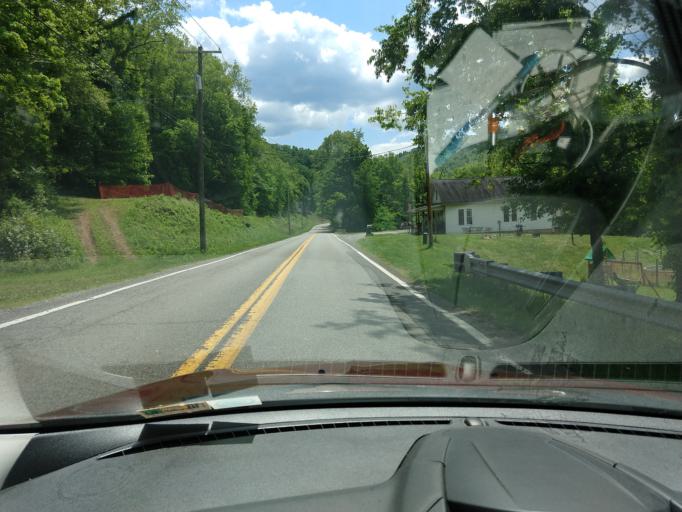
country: US
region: West Virginia
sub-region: Gilmer County
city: Glenville
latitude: 38.8689
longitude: -80.6771
